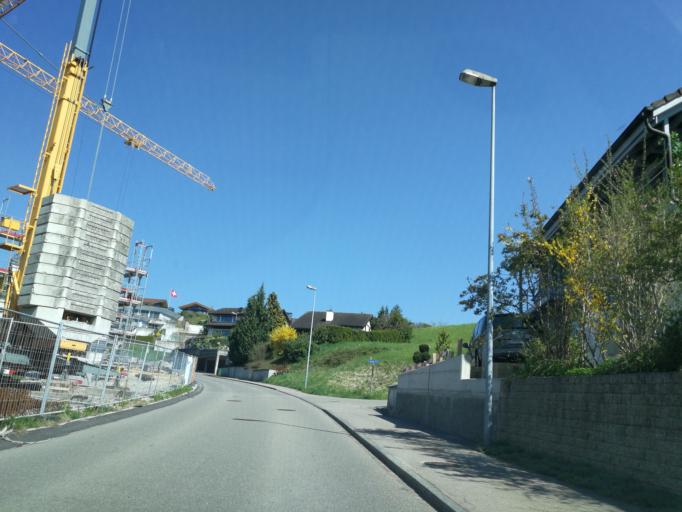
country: CH
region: Saint Gallen
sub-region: Wahlkreis See-Gaster
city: Rapperswil
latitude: 47.2430
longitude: 8.8206
